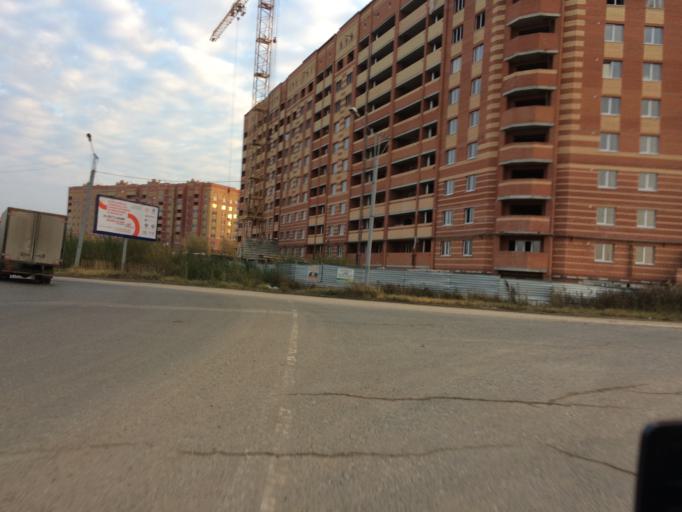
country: RU
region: Mariy-El
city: Yoshkar-Ola
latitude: 56.6438
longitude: 47.9245
